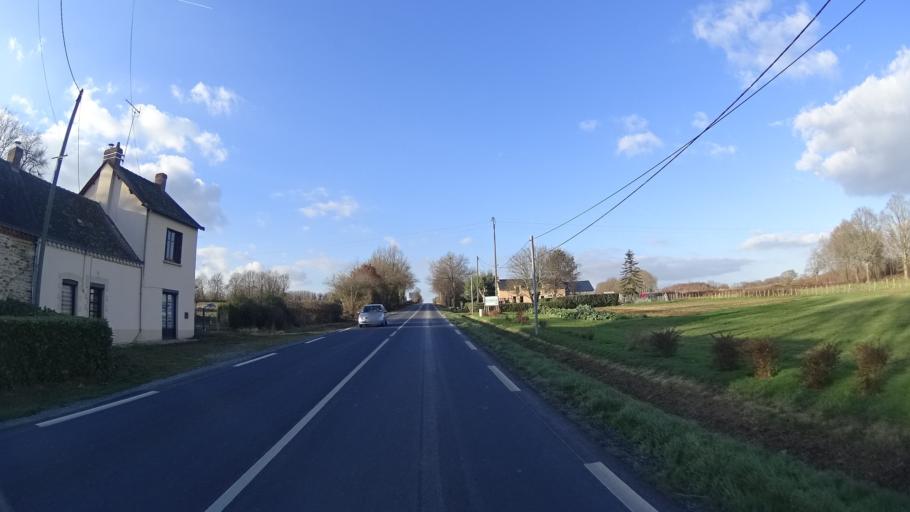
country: FR
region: Pays de la Loire
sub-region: Departement de la Loire-Atlantique
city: Guenrouet
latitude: 47.5451
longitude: -1.9423
